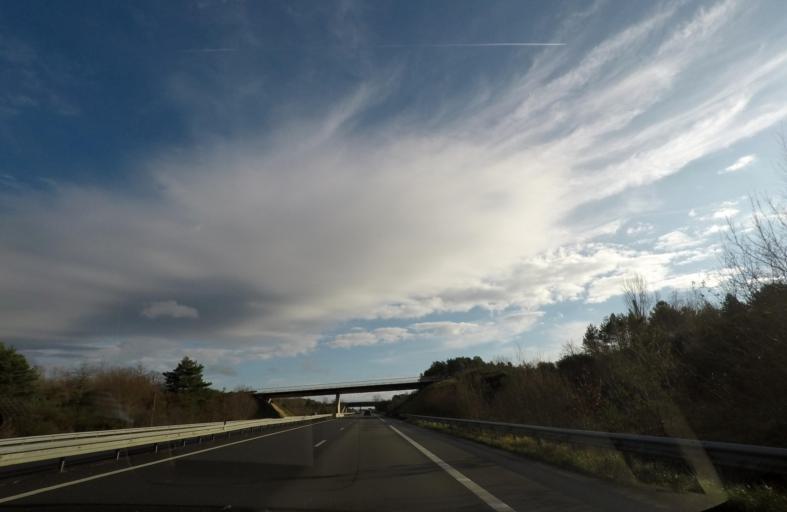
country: FR
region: Centre
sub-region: Departement du Loir-et-Cher
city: Villefranche-sur-Cher
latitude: 47.3120
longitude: 1.8255
